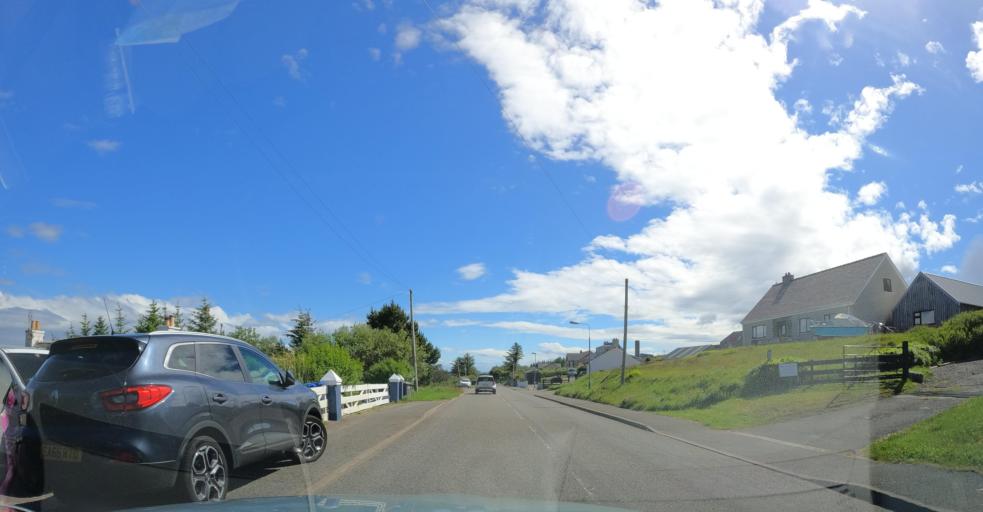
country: GB
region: Scotland
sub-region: Eilean Siar
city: Isle of Lewis
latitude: 58.2439
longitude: -6.3914
